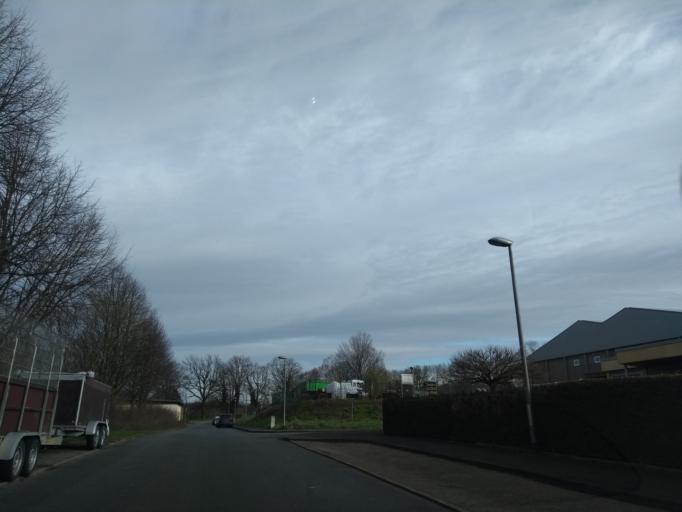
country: DE
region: North Rhine-Westphalia
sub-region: Regierungsbezirk Detmold
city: Detmold
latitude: 51.9538
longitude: 8.8971
